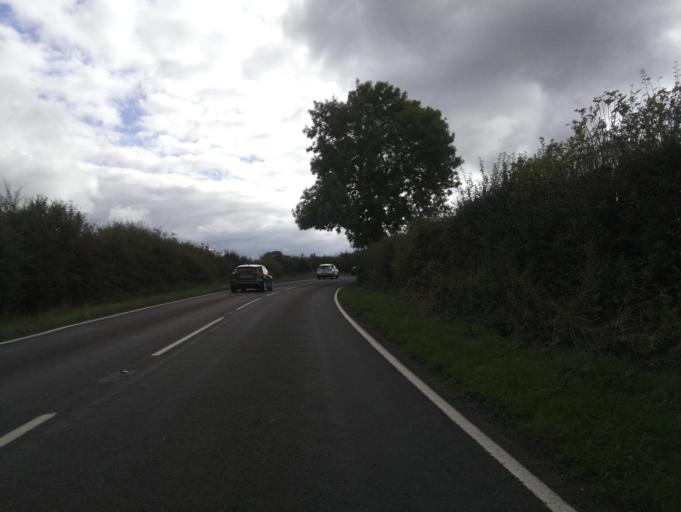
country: GB
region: England
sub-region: Leicestershire
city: Coalville
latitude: 52.7578
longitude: -1.3781
